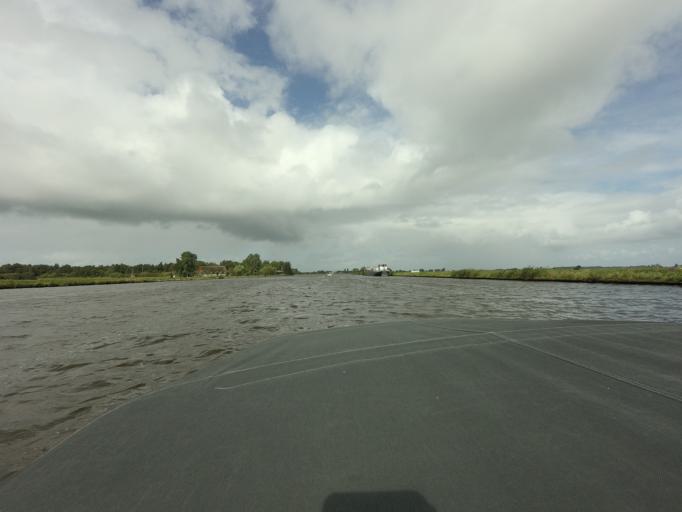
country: NL
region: Friesland
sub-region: Gemeente Boarnsterhim
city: Warten
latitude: 53.1367
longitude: 5.9167
